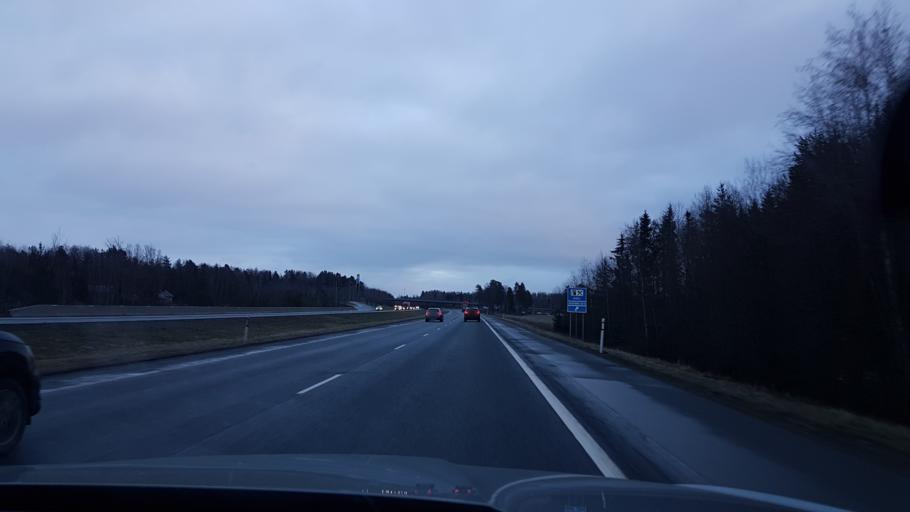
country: FI
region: Haeme
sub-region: Haemeenlinna
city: Kalvola
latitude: 61.1018
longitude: 24.1567
